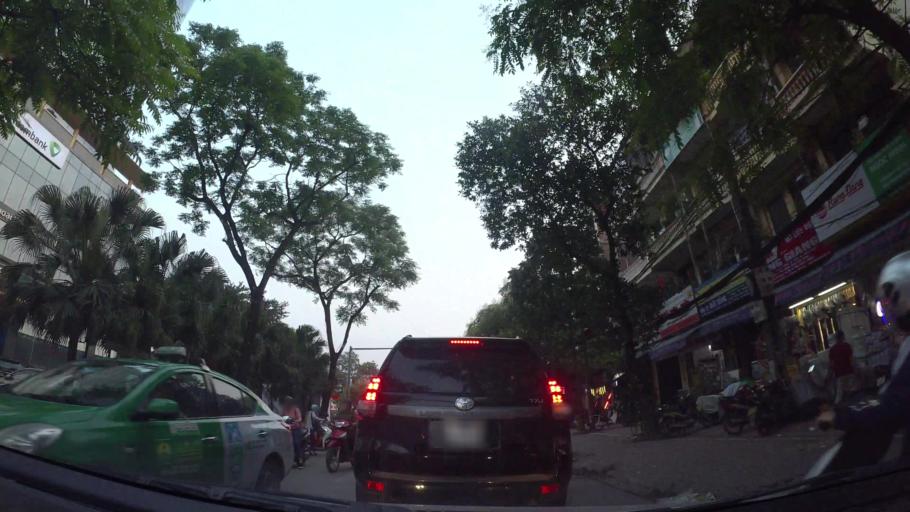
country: VN
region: Ha Noi
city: Cau Giay
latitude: 21.0468
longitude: 105.7902
